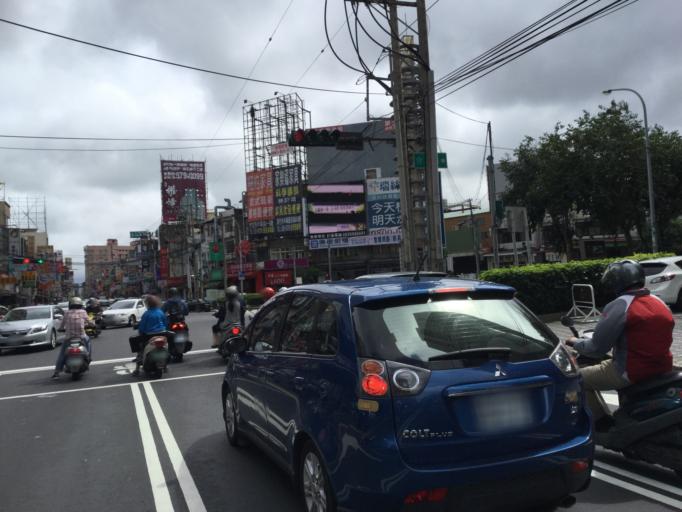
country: TW
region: Taiwan
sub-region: Hsinchu
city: Hsinchu
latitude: 24.7820
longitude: 121.0205
